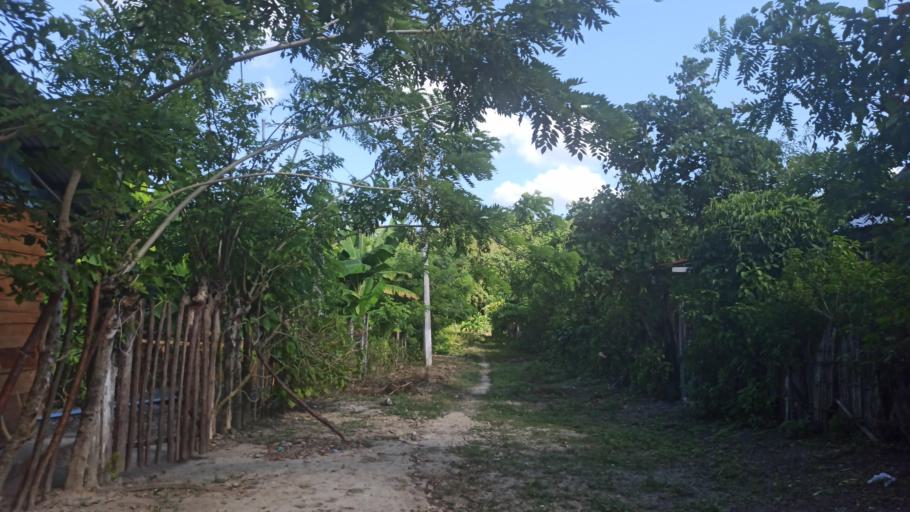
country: MX
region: Veracruz
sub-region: Papantla
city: Residencial Tajin
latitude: 20.6434
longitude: -97.3644
